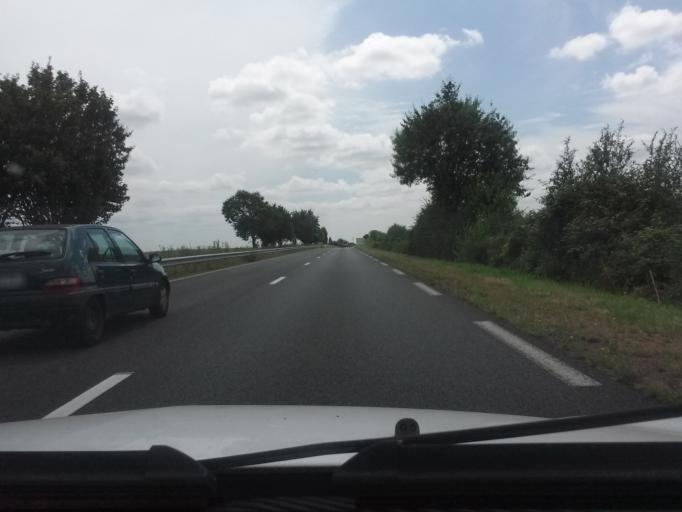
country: FR
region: Pays de la Loire
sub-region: Departement de la Vendee
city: Saint-Andre-Treize-Voies
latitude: 46.8865
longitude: -1.3901
